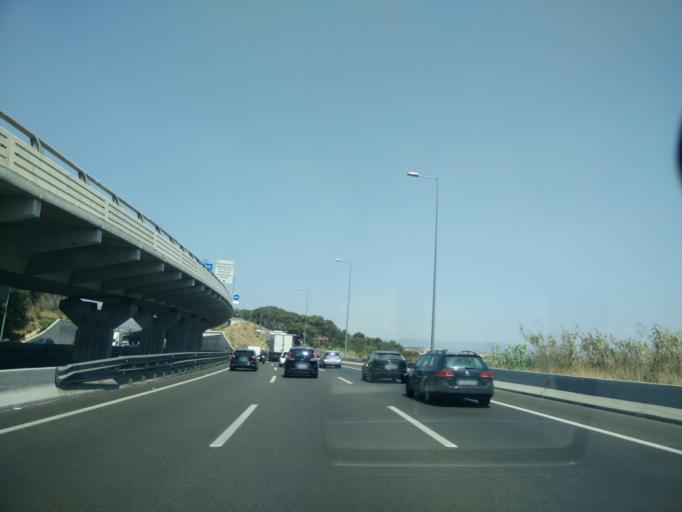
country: ES
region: Catalonia
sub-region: Provincia de Barcelona
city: Ripollet
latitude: 41.4764
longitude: 2.1631
